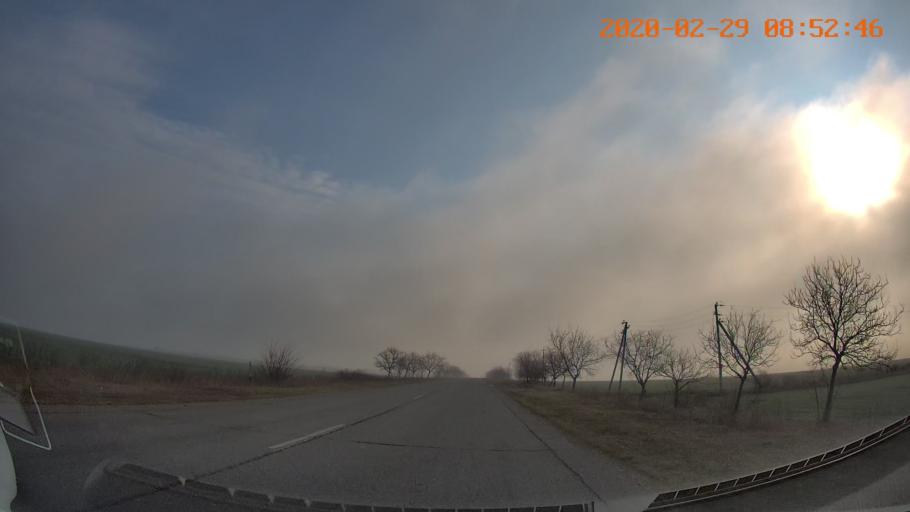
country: MD
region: Anenii Noi
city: Varnita
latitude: 46.9243
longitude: 29.5441
